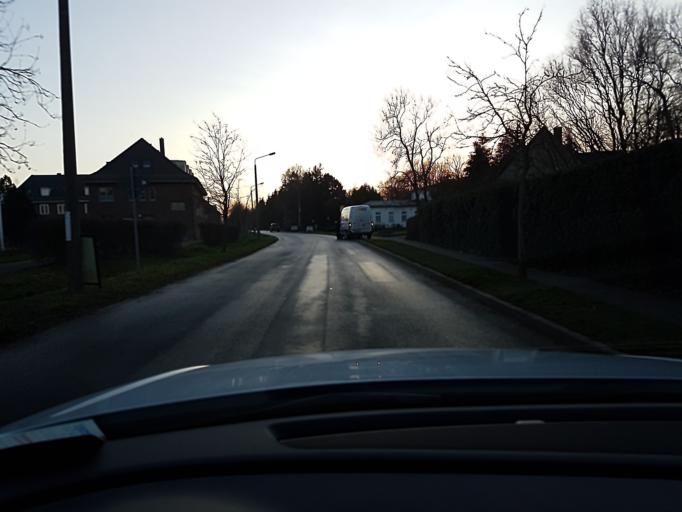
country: DE
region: Mecklenburg-Vorpommern
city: Wiek
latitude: 54.6184
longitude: 13.2874
